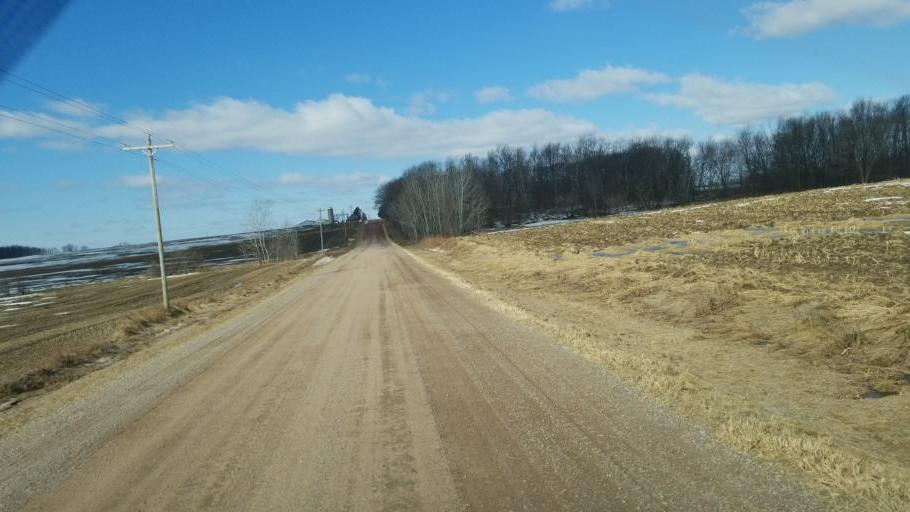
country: US
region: Wisconsin
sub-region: Clark County
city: Loyal
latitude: 44.6834
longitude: -90.4515
